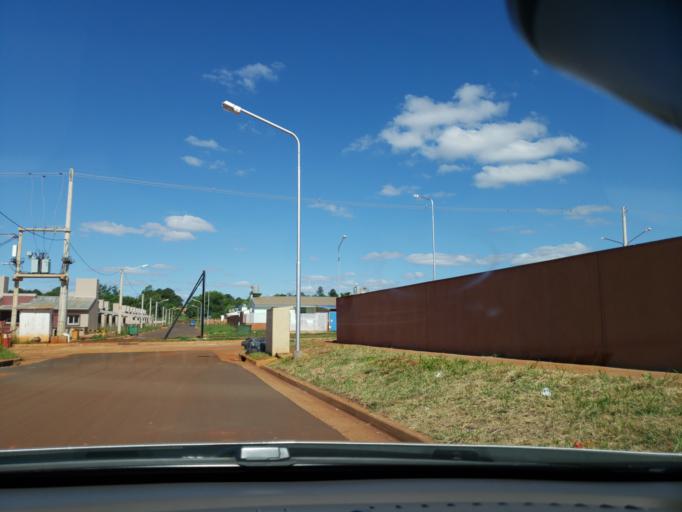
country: AR
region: Misiones
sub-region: Departamento de Capital
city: Posadas
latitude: -27.4044
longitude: -55.9814
